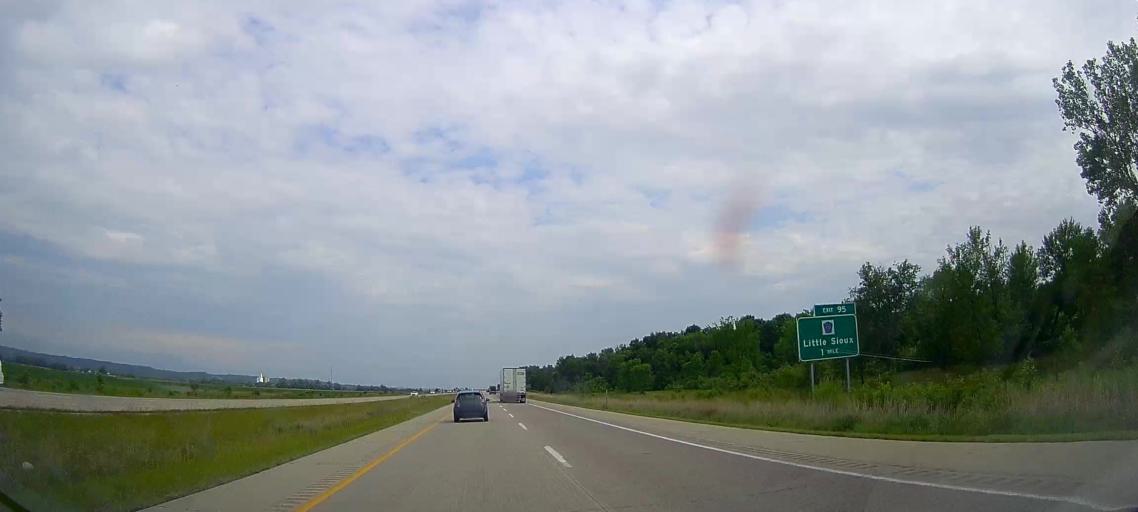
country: US
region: Nebraska
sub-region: Burt County
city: Tekamah
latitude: 41.8163
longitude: -96.0685
